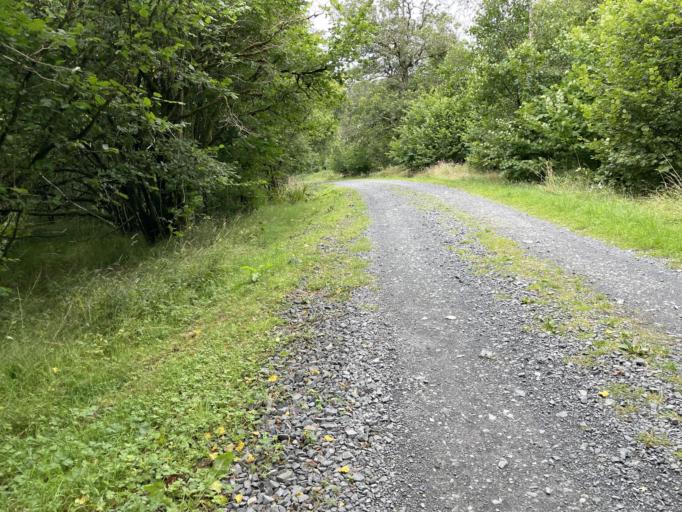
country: GB
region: Scotland
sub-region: Dumfries and Galloway
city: Newton Stewart
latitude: 55.0791
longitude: -4.5096
